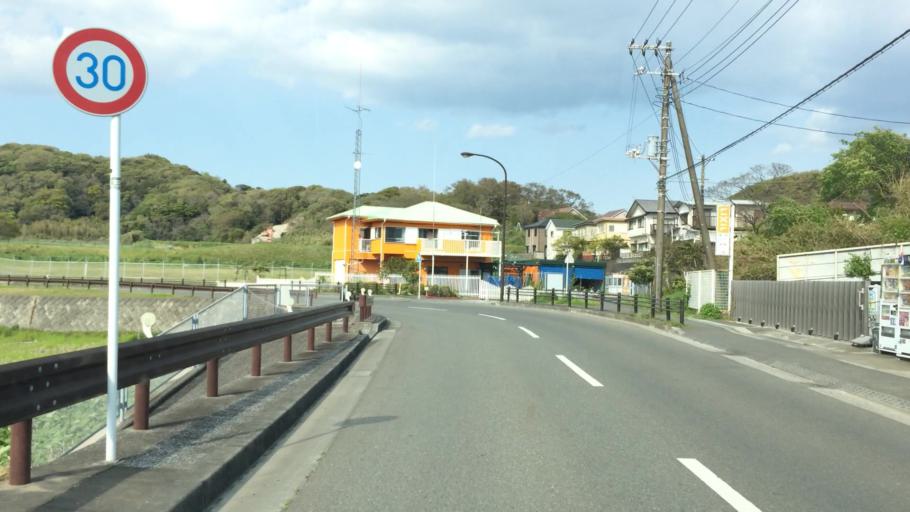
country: JP
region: Kanagawa
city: Yokosuka
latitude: 35.2305
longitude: 139.6303
